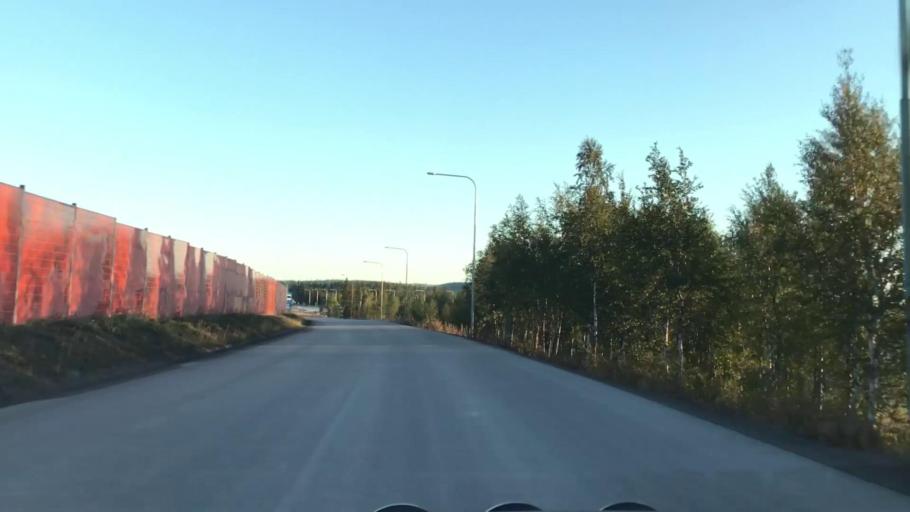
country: SE
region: Norrbotten
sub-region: Gallivare Kommun
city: Malmberget
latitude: 67.6500
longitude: 21.0186
